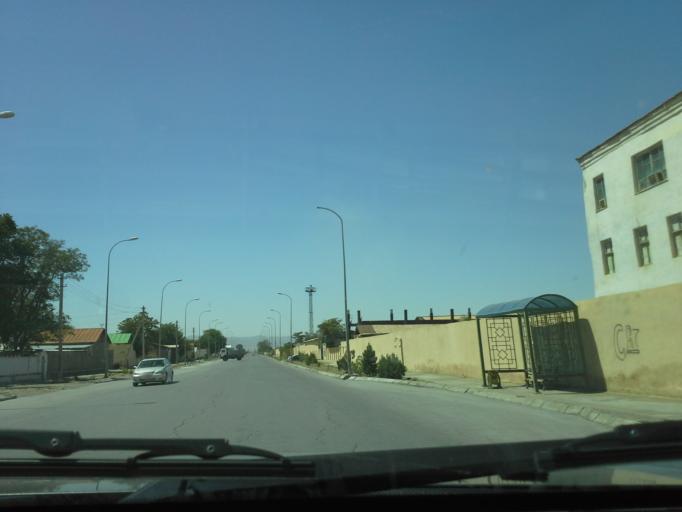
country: TM
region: Balkan
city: Serdar
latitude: 38.9774
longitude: 56.2714
